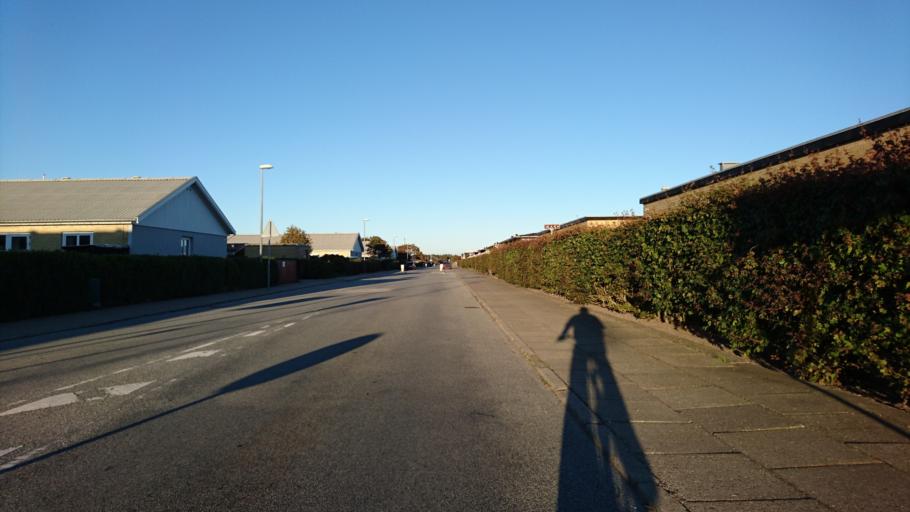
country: DK
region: North Denmark
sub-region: Frederikshavn Kommune
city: Skagen
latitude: 57.7305
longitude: 10.5831
